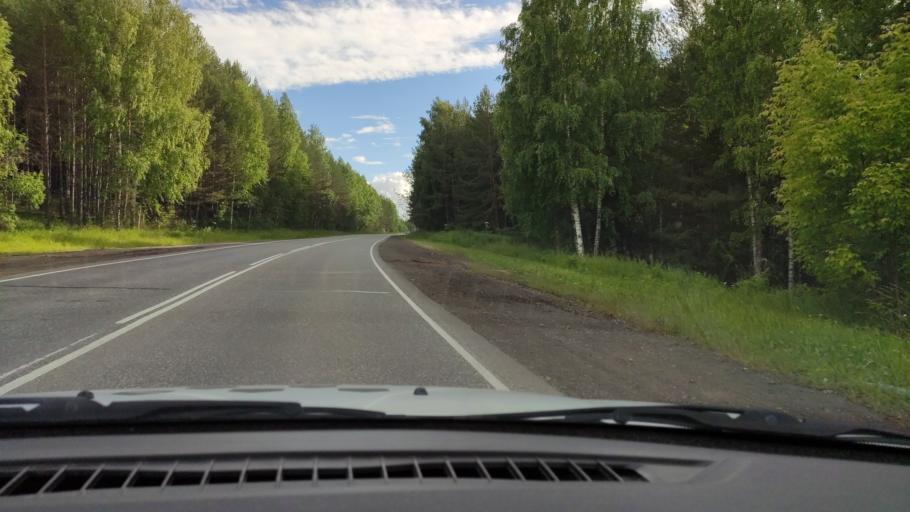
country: RU
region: Perm
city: Kungur
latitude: 57.4136
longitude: 56.9126
